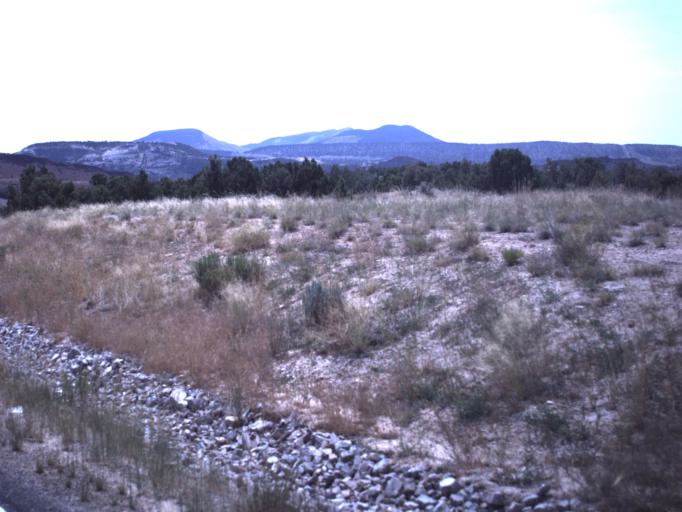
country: US
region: Utah
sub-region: Uintah County
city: Vernal
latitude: 40.6089
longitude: -109.4698
